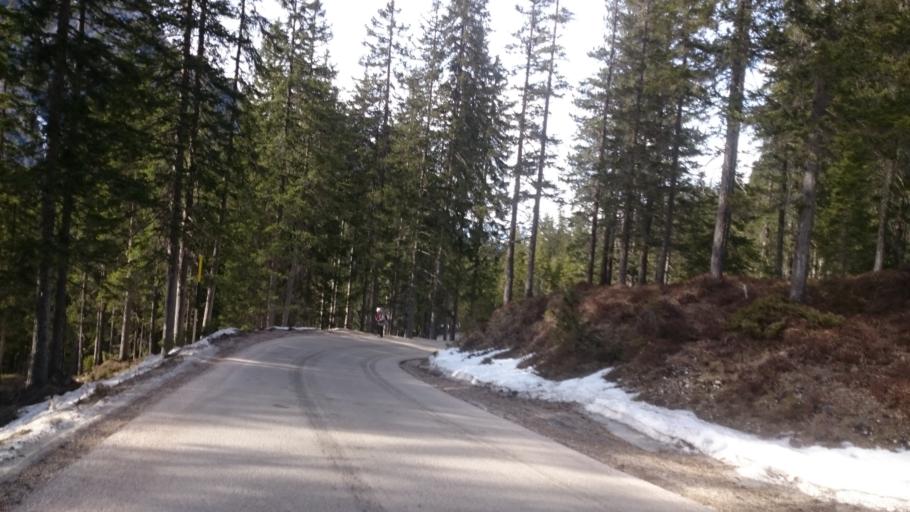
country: IT
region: Trentino-Alto Adige
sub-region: Bolzano
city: Braies
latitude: 46.6723
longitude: 12.1578
